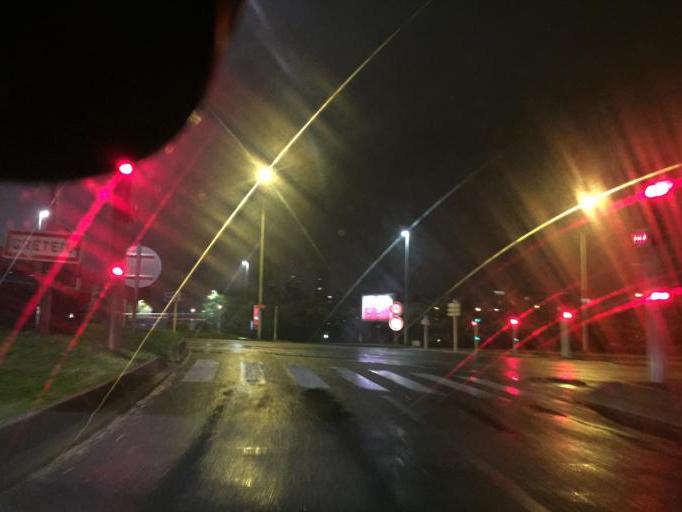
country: FR
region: Ile-de-France
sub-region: Departement du Val-de-Marne
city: Creteil
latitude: 48.7774
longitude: 2.4603
